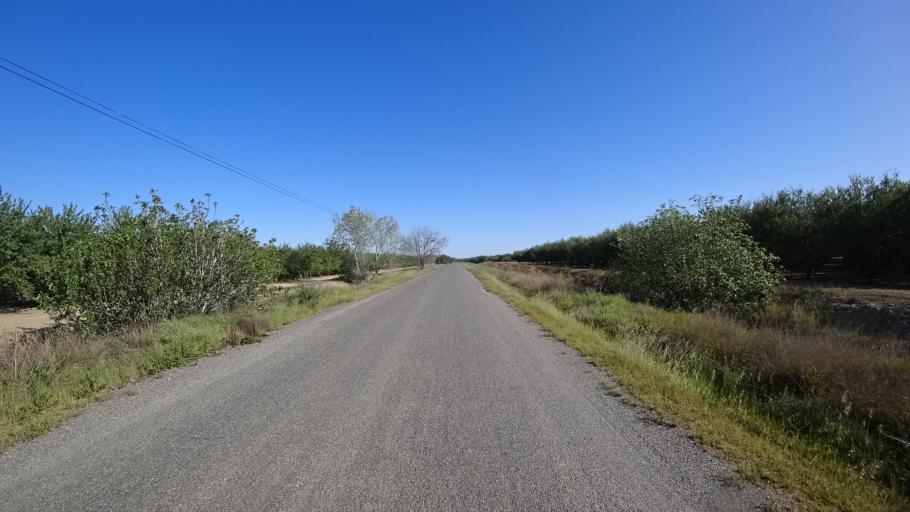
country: US
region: California
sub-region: Glenn County
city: Hamilton City
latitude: 39.7024
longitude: -122.0548
